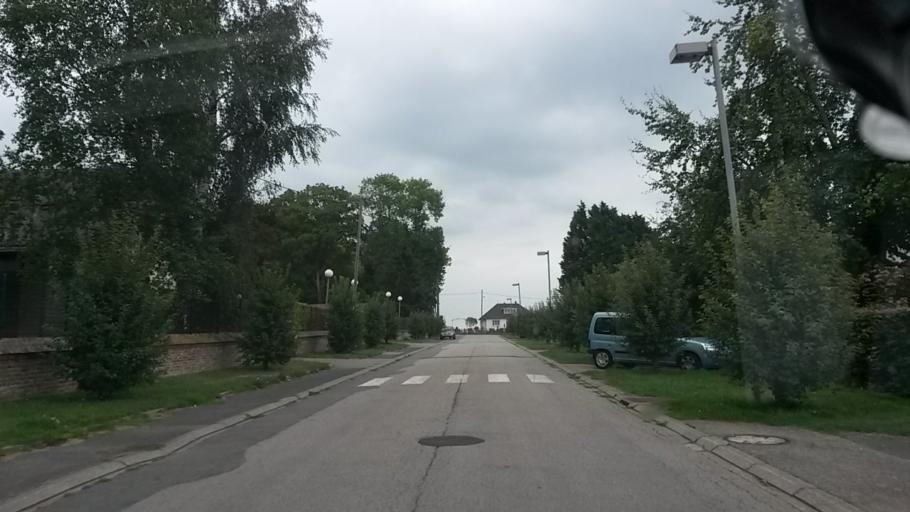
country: FR
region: Haute-Normandie
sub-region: Departement de la Seine-Maritime
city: Forges-les-Eaux
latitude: 49.6056
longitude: 1.5452
